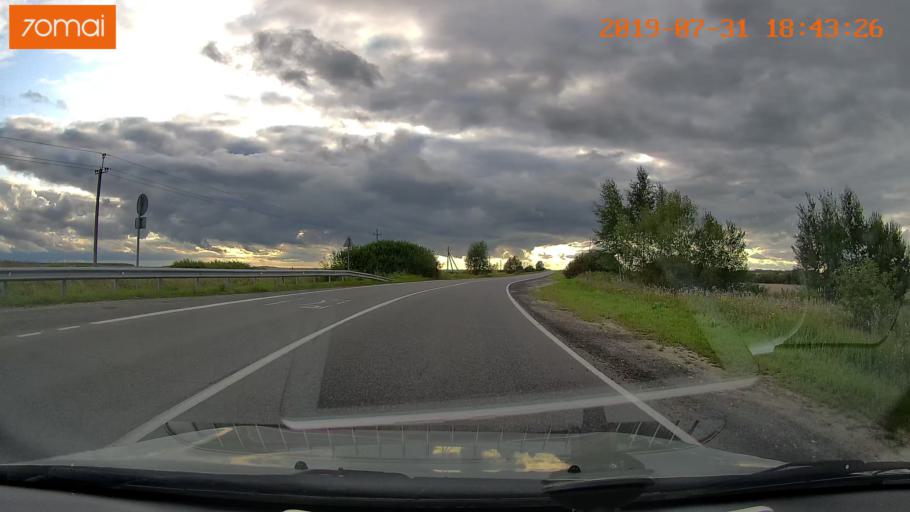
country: RU
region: Moskovskaya
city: Troitskoye
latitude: 55.2445
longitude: 38.5749
